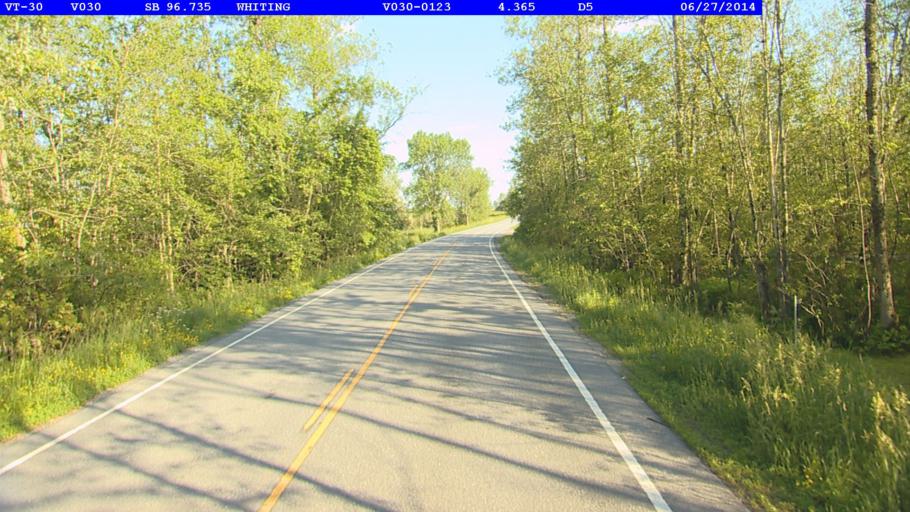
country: US
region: Vermont
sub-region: Addison County
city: Middlebury (village)
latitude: 43.9000
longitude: -73.2052
